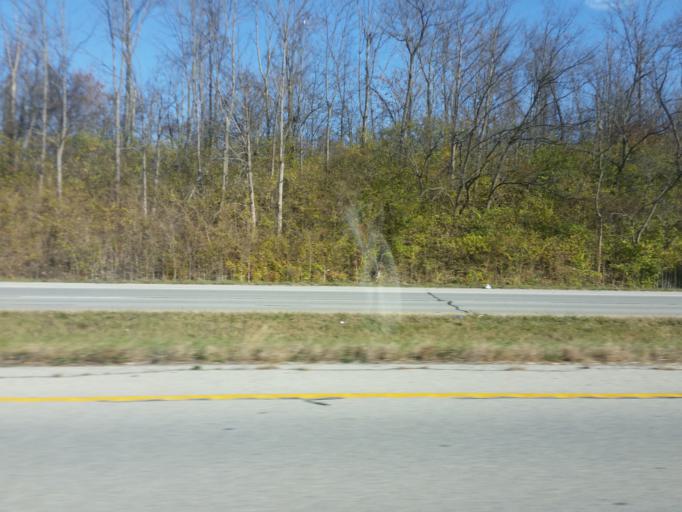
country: US
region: Ohio
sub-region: Hamilton County
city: Dunlap
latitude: 39.2891
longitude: -84.6063
